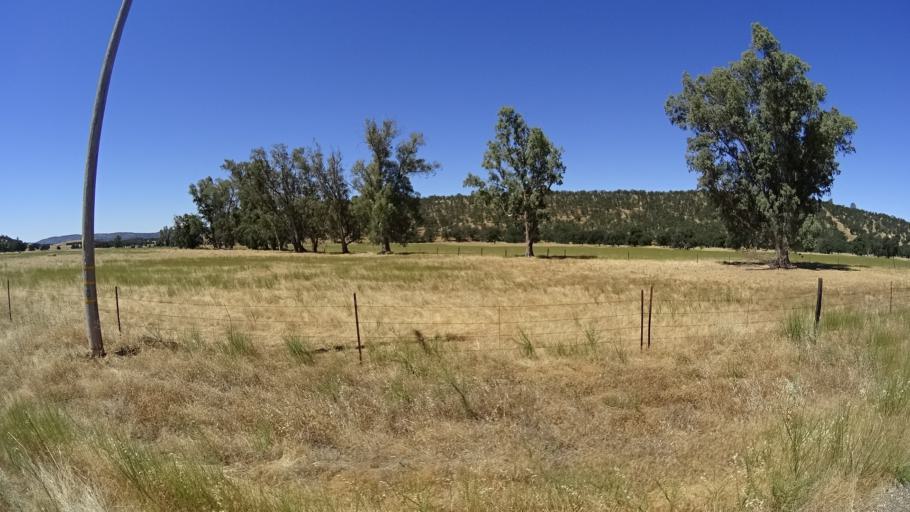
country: US
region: California
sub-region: Calaveras County
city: Copperopolis
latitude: 38.0170
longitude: -120.6769
